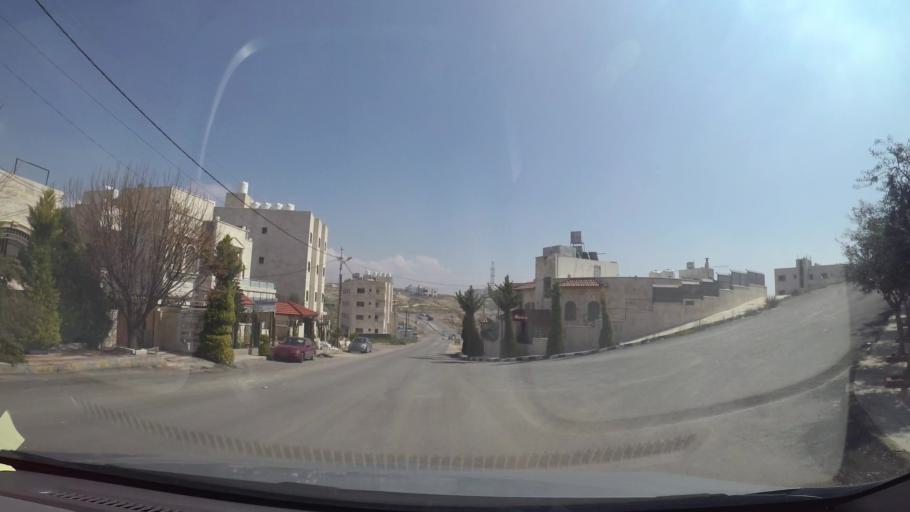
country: JO
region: Amman
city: Al Bunayyat ash Shamaliyah
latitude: 31.8889
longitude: 35.8996
